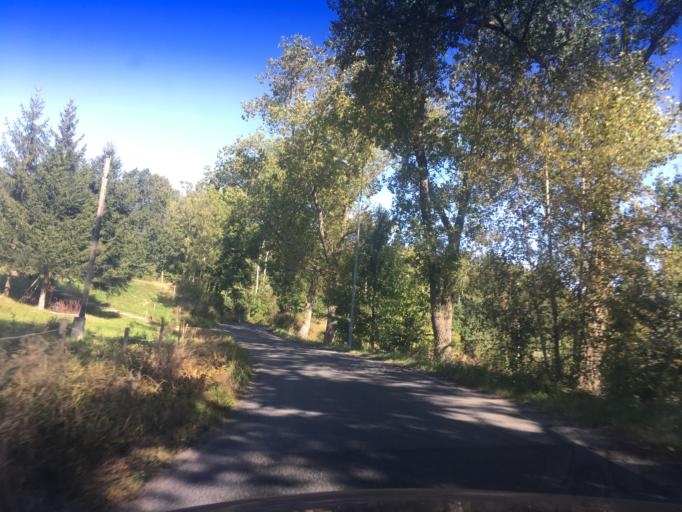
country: PL
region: Lower Silesian Voivodeship
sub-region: Powiat lubanski
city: Lesna
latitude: 51.0305
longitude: 15.2269
